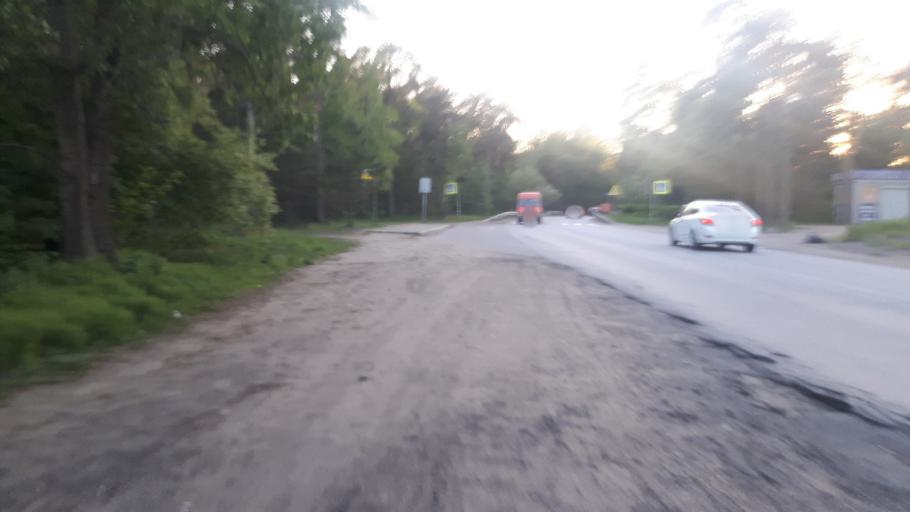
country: RU
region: St.-Petersburg
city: Bol'shaya Izhora
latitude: 59.9444
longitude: 29.5732
